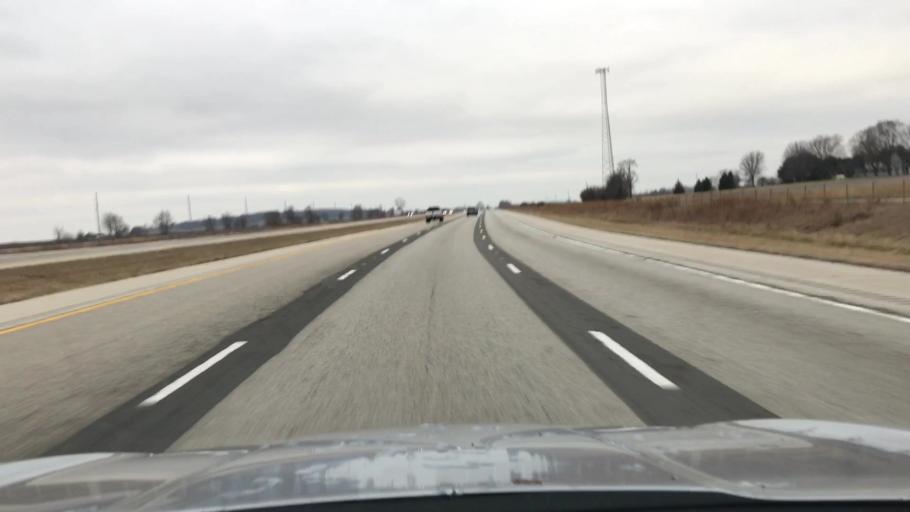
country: US
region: Illinois
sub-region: Logan County
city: Lincoln
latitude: 40.0599
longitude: -89.4517
